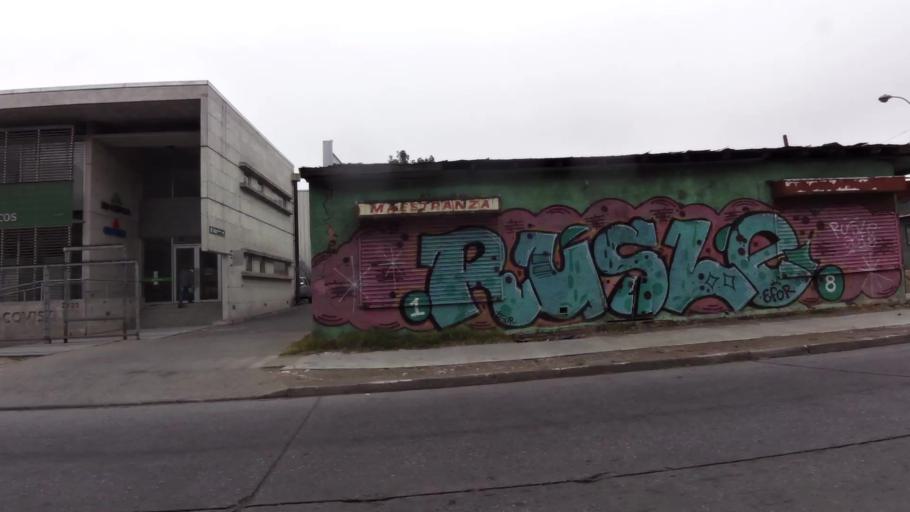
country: CL
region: Biobio
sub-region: Provincia de Concepcion
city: Concepcion
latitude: -36.8117
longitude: -73.0364
